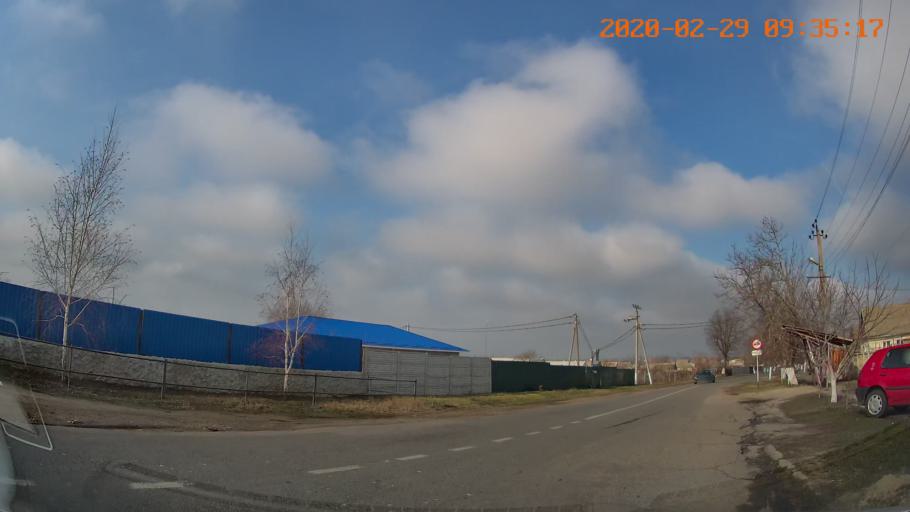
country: MD
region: Telenesti
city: Dnestrovsc
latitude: 46.6184
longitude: 29.9008
